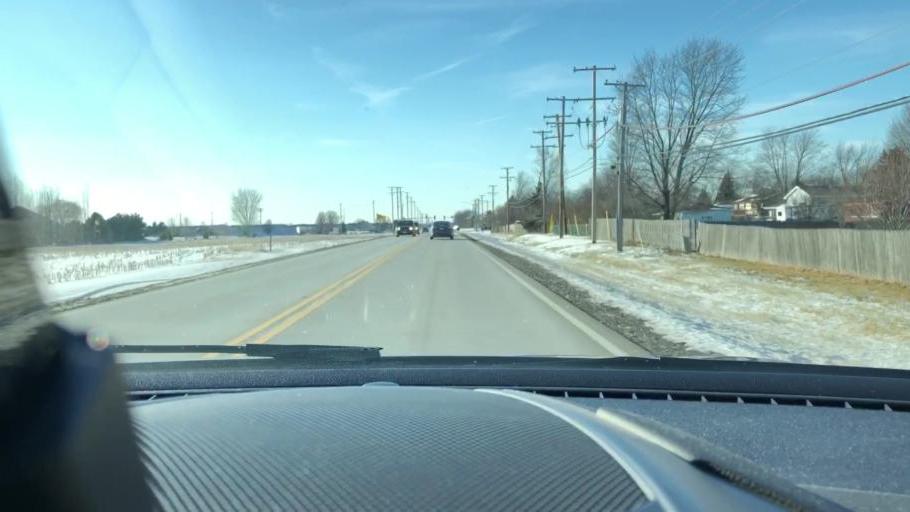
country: US
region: Illinois
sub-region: Will County
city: New Lenox
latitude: 41.4836
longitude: -87.9362
